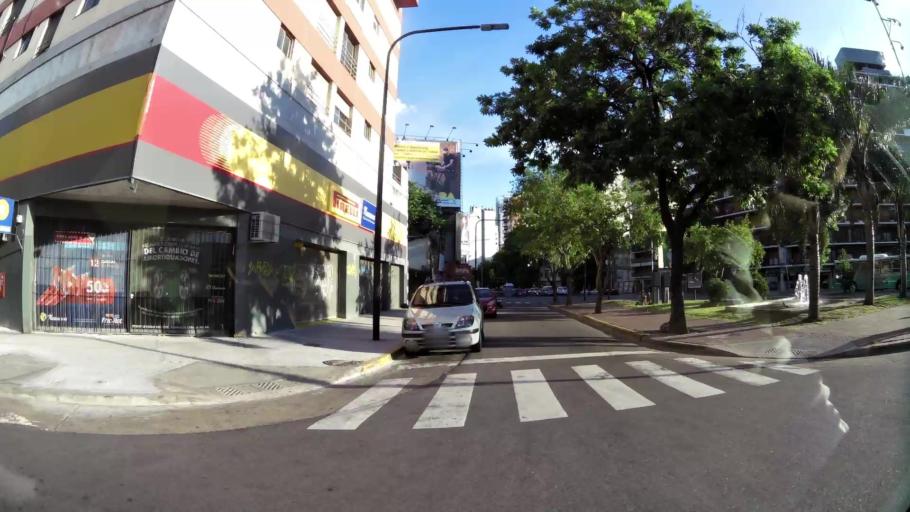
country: AR
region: Buenos Aires F.D.
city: Colegiales
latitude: -34.6074
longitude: -58.4453
